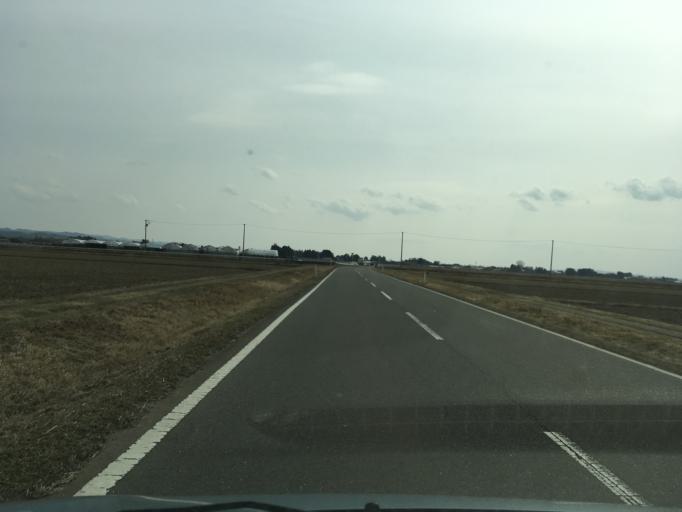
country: JP
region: Miyagi
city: Wakuya
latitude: 38.7302
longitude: 141.2395
